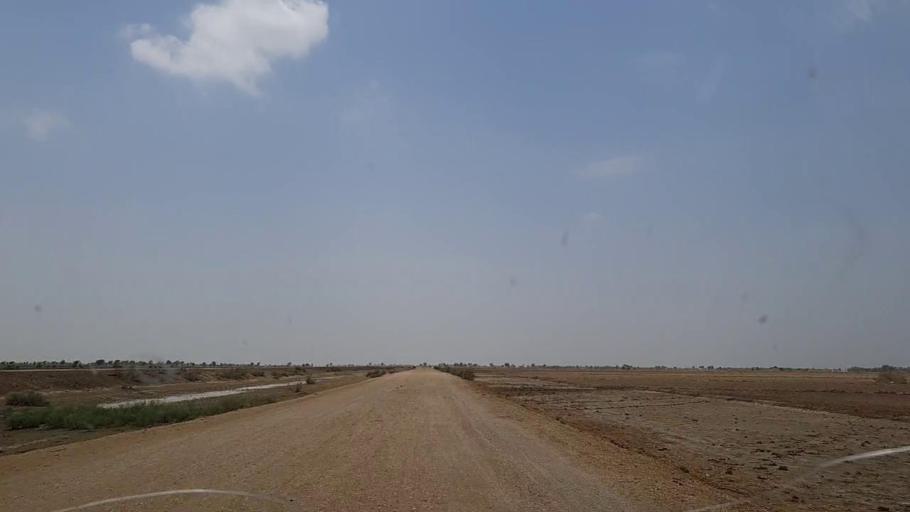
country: PK
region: Sindh
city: Phulji
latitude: 26.7930
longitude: 67.6413
